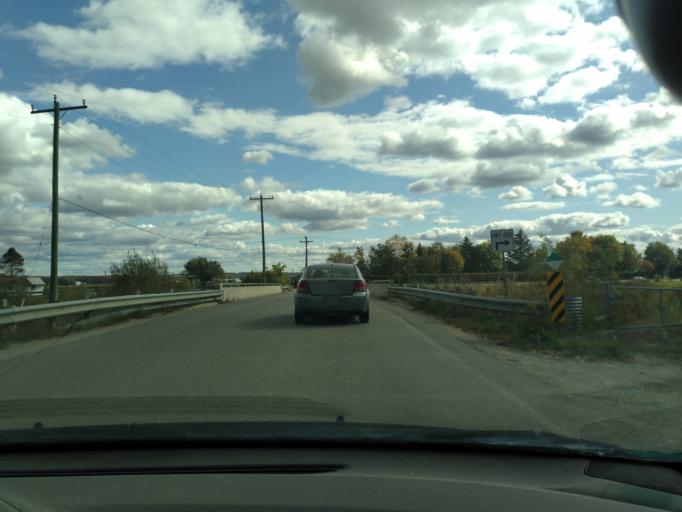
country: CA
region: Ontario
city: Bradford West Gwillimbury
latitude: 44.0846
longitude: -79.5777
